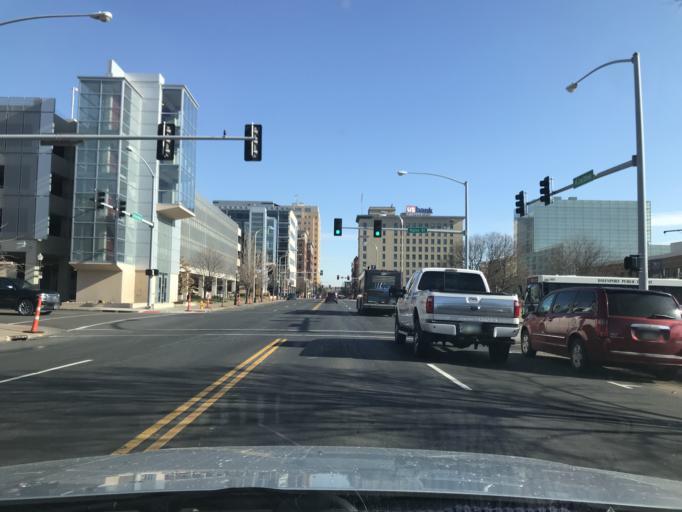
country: US
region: Iowa
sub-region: Scott County
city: Davenport
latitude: 41.5214
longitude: -90.5789
